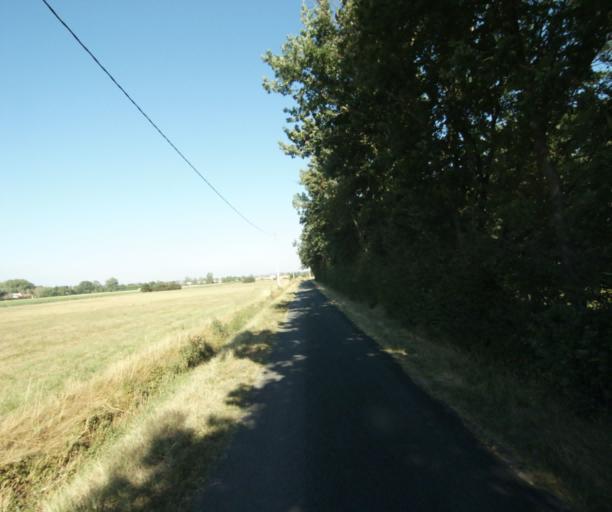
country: FR
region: Midi-Pyrenees
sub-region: Departement de la Haute-Garonne
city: Revel
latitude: 43.4617
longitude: 2.0253
